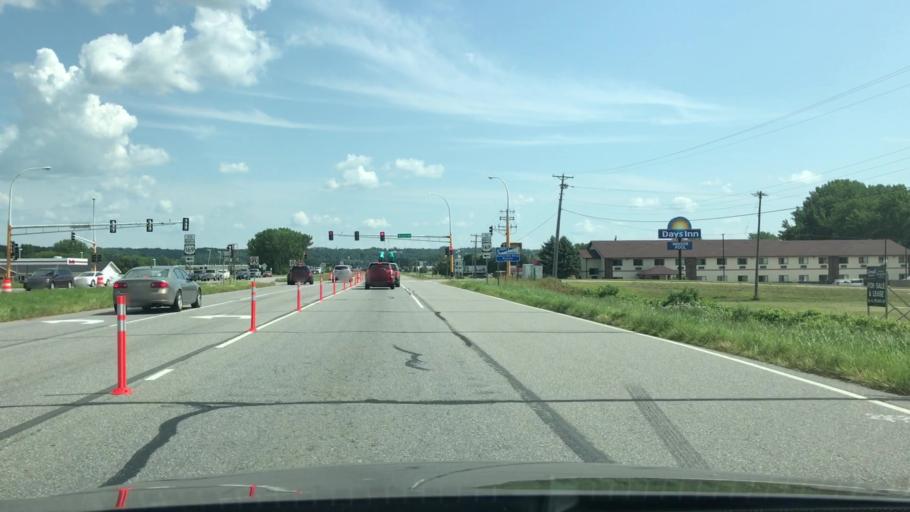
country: US
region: Minnesota
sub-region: Nicollet County
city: North Mankato
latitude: 44.1891
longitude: -94.0150
